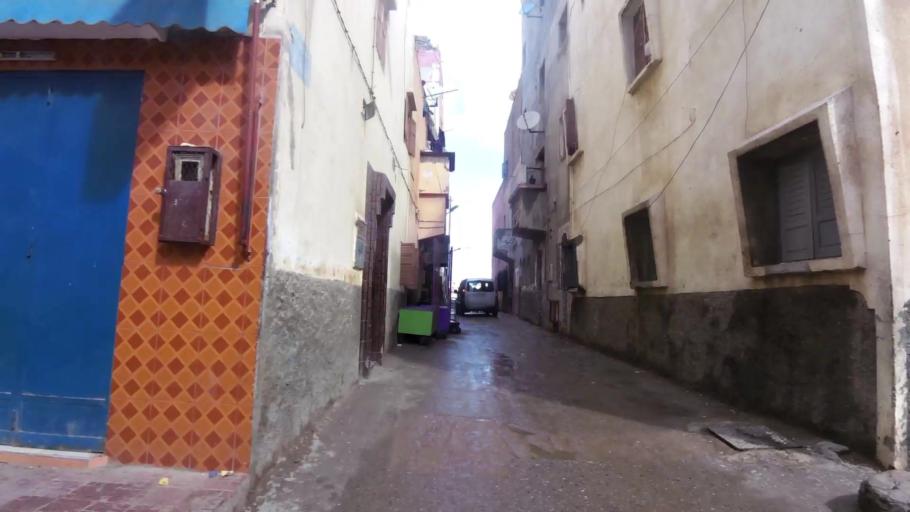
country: MA
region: Grand Casablanca
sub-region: Casablanca
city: Casablanca
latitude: 33.5320
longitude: -7.6694
